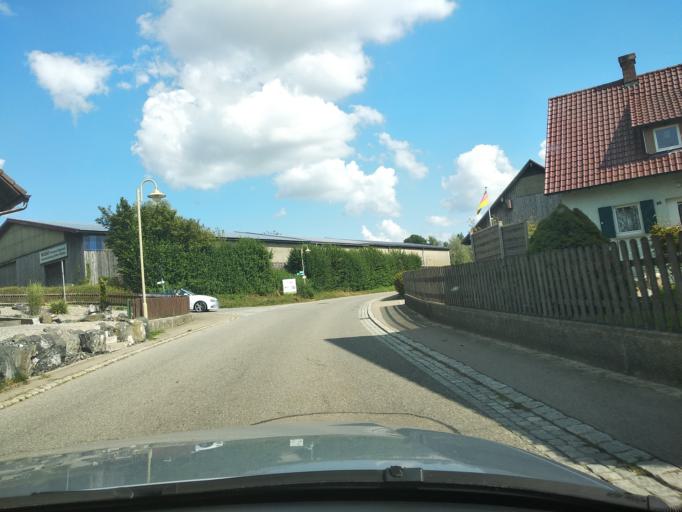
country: DE
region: Baden-Wuerttemberg
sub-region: Tuebingen Region
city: Leutkirch im Allgau
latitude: 47.8896
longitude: 9.9744
